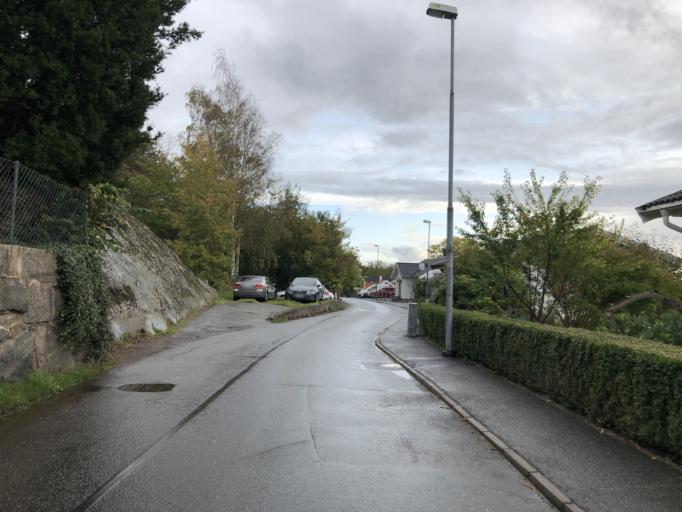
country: SE
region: Vaestra Goetaland
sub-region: Molndal
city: Moelndal
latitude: 57.6527
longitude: 12.0308
